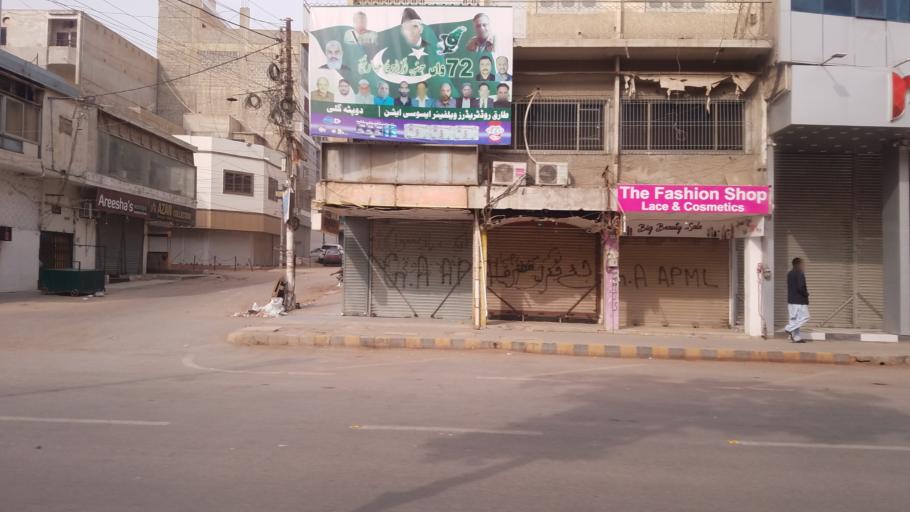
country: PK
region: Sindh
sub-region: Karachi District
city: Karachi
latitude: 24.8729
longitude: 67.0605
